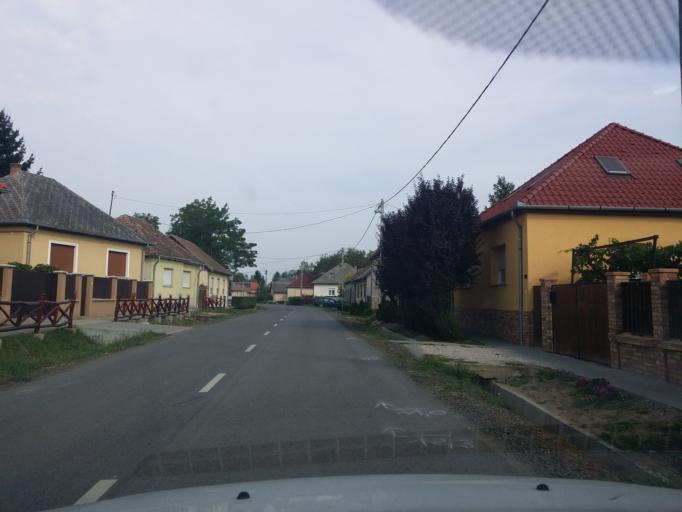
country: HU
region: Pest
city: Acsa
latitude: 47.7766
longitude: 19.3665
